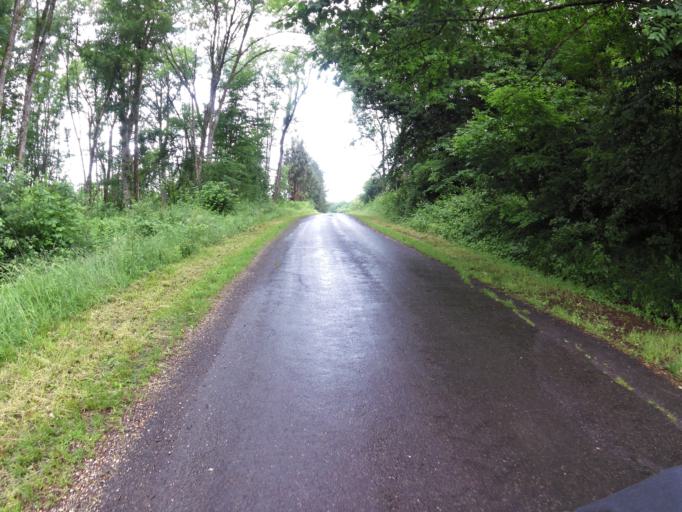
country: FR
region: Champagne-Ardenne
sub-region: Departement de la Marne
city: Sermaize-les-Bains
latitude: 48.7748
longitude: 4.9231
